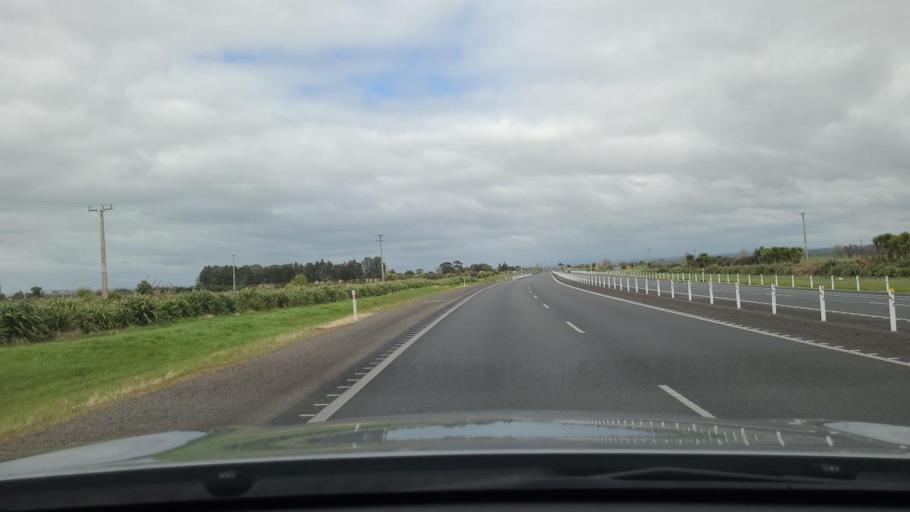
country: NZ
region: Bay of Plenty
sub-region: Western Bay of Plenty District
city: Maketu
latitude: -37.7375
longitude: 176.3506
